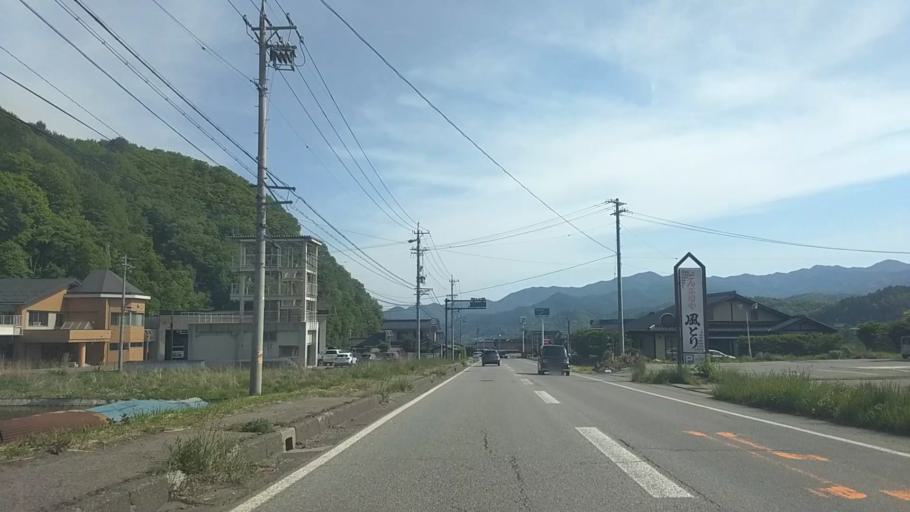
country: JP
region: Nagano
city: Saku
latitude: 36.0694
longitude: 138.4752
